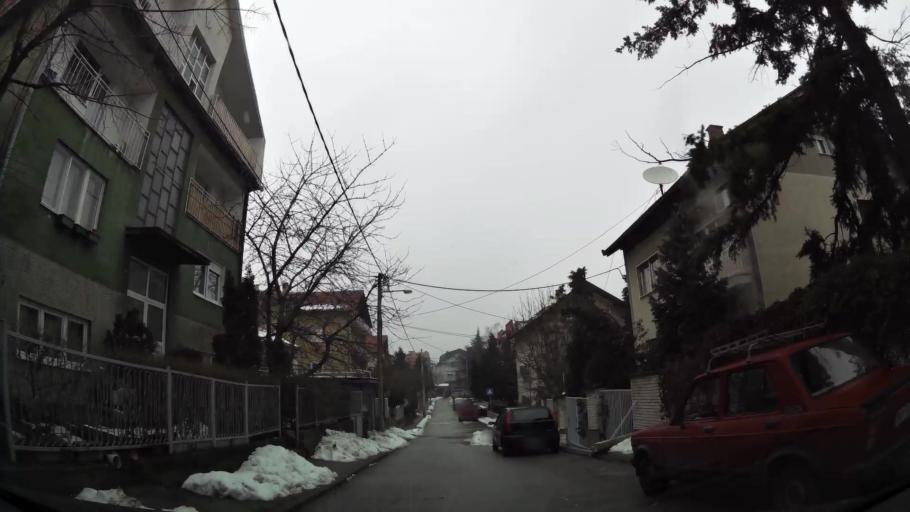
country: RS
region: Central Serbia
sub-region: Belgrade
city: Vozdovac
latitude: 44.7717
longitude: 20.4805
